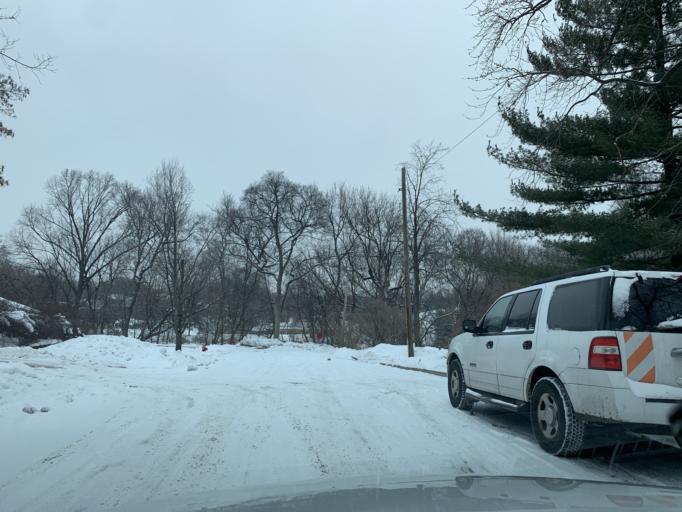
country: US
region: Minnesota
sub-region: Hennepin County
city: Saint Louis Park
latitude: 44.9202
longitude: -93.3426
